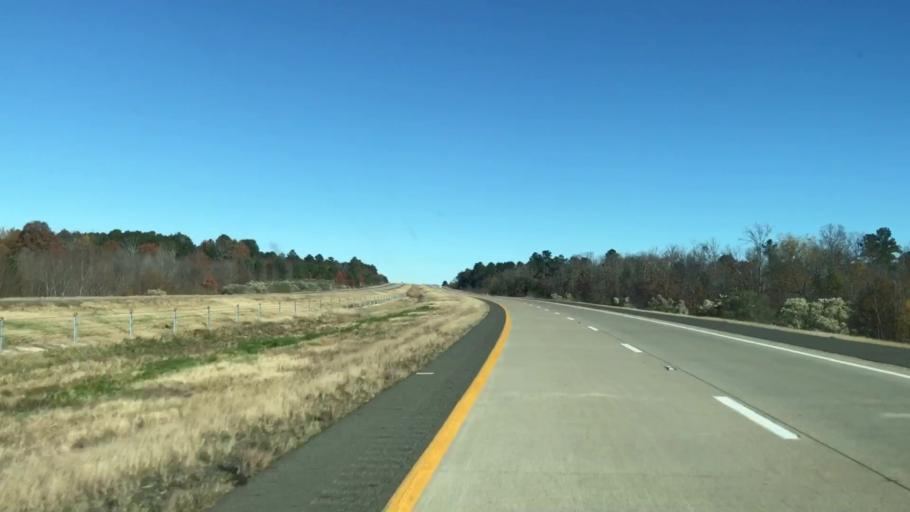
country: US
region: Texas
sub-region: Cass County
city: Queen City
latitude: 33.1709
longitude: -93.8779
